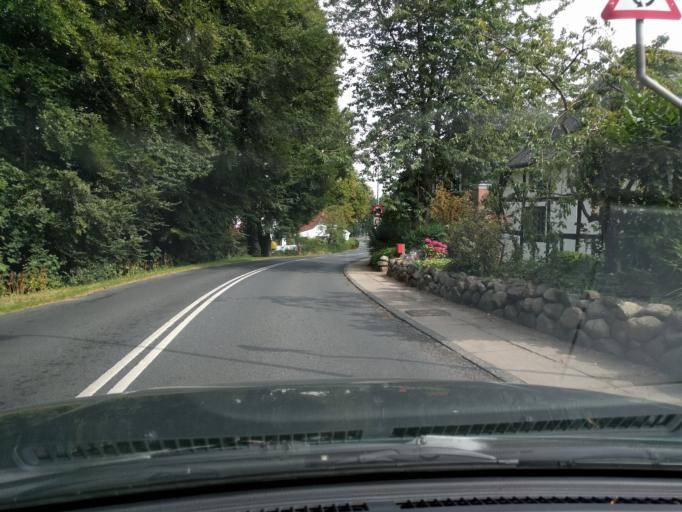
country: DK
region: South Denmark
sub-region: Odense Kommune
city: Bullerup
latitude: 55.3985
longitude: 10.4613
